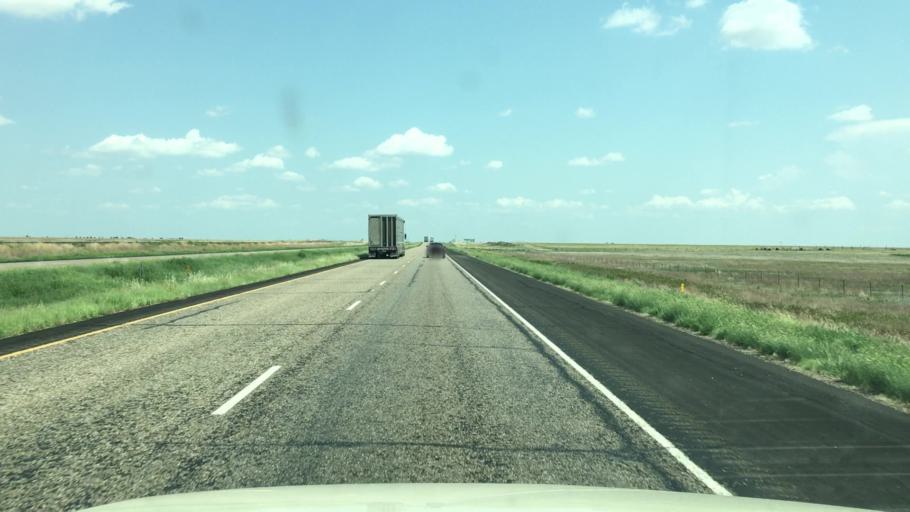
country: US
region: Texas
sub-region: Armstrong County
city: Claude
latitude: 35.1324
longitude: -101.4206
